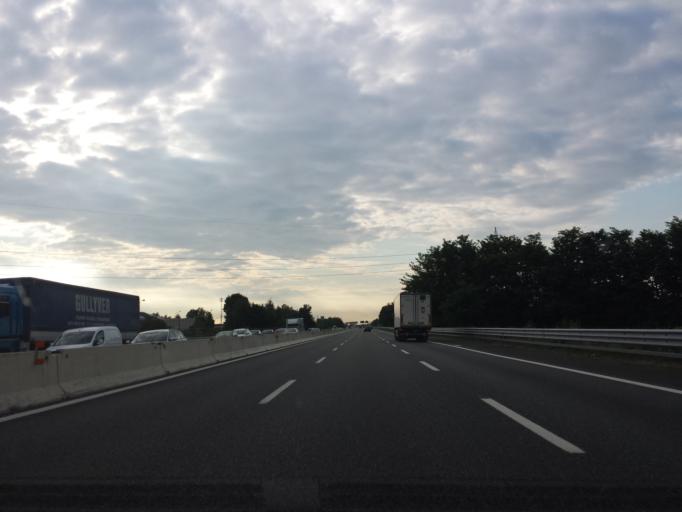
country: IT
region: Lombardy
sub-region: Provincia di Varese
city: Cassano Magnago
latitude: 45.6568
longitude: 8.8171
